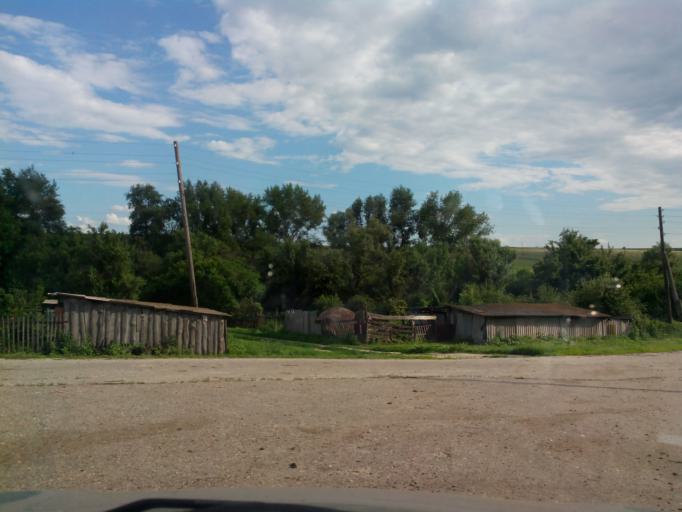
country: RU
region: Volgograd
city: Slashchevskaya
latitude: 49.7754
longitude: 42.4409
